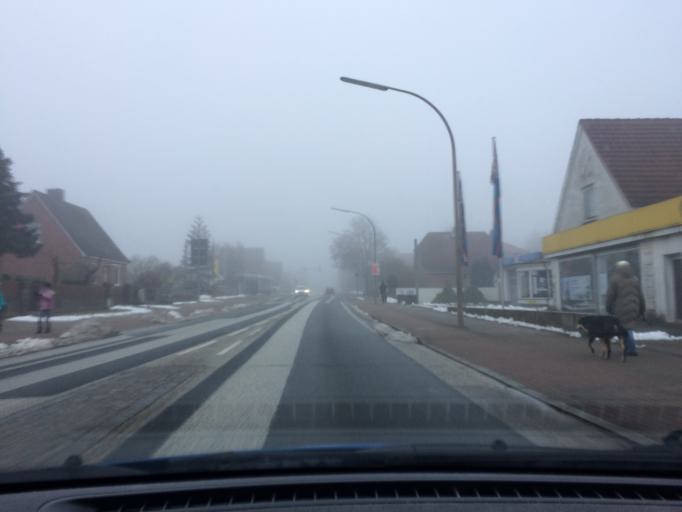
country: DE
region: Schleswig-Holstein
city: Schwarzenbek
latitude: 53.5067
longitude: 10.4811
